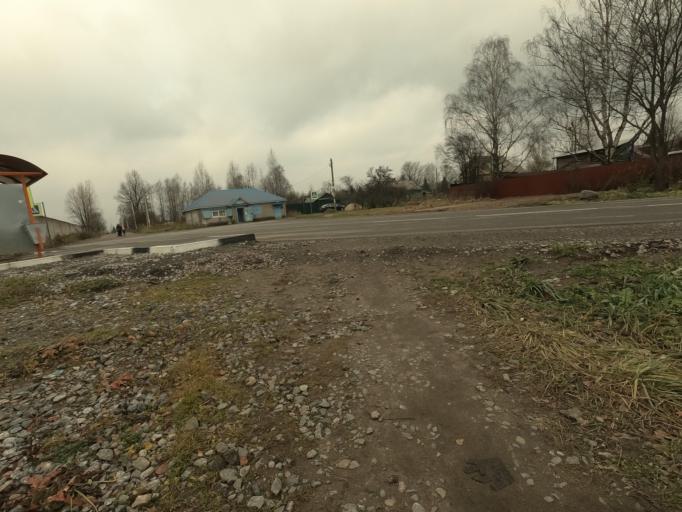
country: RU
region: Leningrad
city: Lyuban'
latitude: 59.4947
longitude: 31.2746
